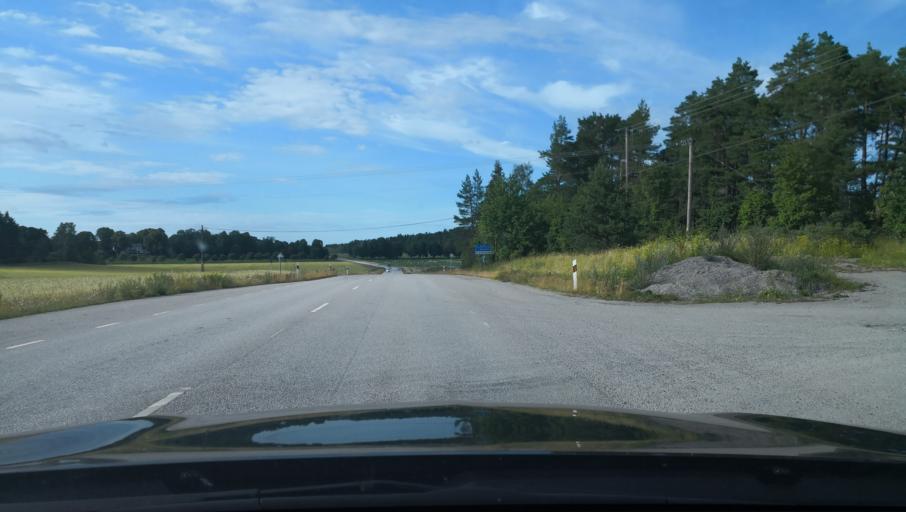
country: SE
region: Uppsala
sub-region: Habo Kommun
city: Balsta
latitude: 59.6103
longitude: 17.5006
